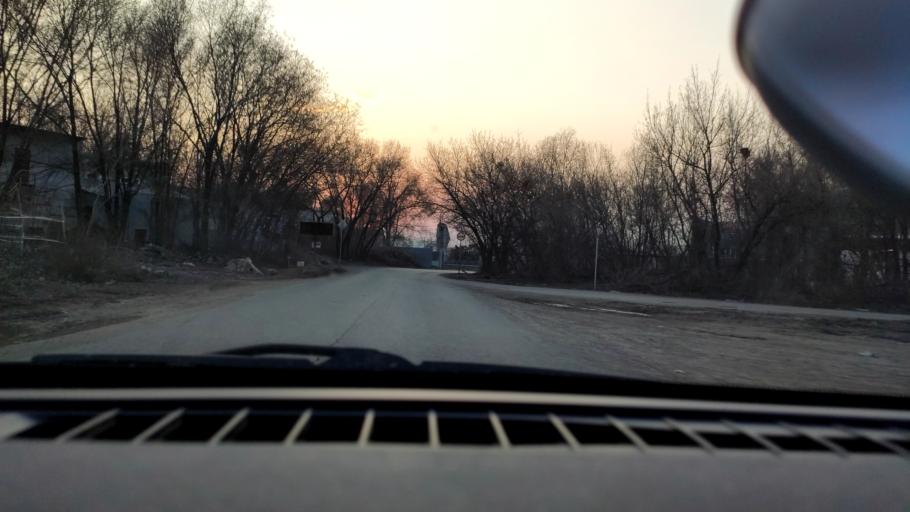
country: RU
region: Samara
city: Smyshlyayevka
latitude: 53.2076
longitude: 50.3094
